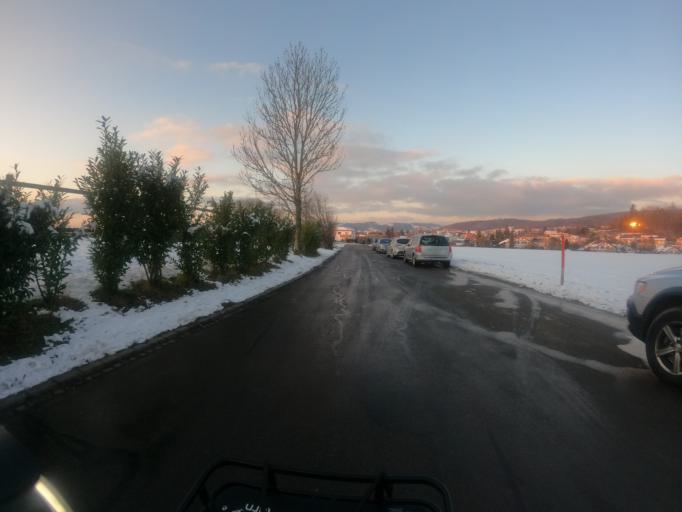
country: CH
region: Zurich
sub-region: Bezirk Affoltern
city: Affoltern / Hasenbueel
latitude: 47.2690
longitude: 8.4507
